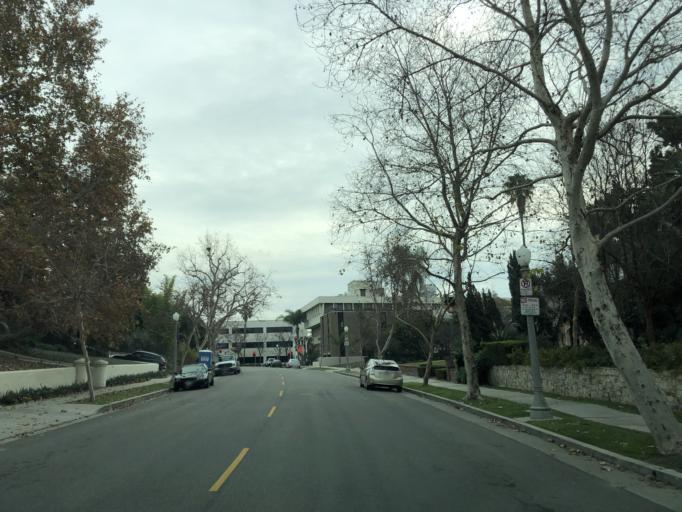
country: US
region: California
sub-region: Los Angeles County
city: Hollywood
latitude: 34.0635
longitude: -118.3348
